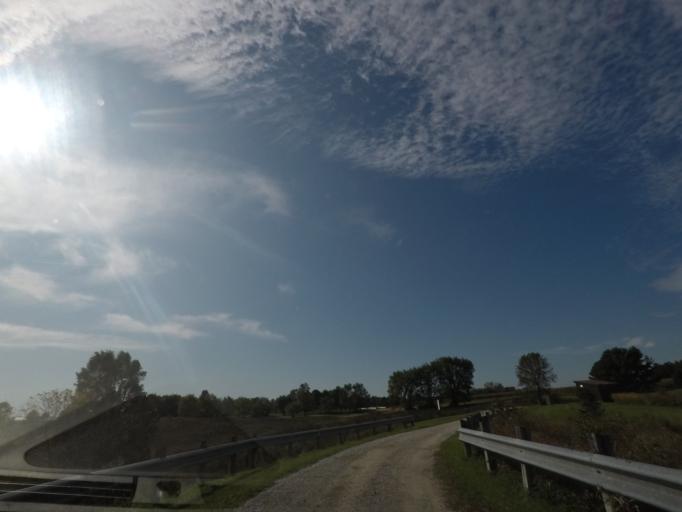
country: US
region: Iowa
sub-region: Story County
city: Gilbert
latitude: 42.1099
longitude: -93.5821
